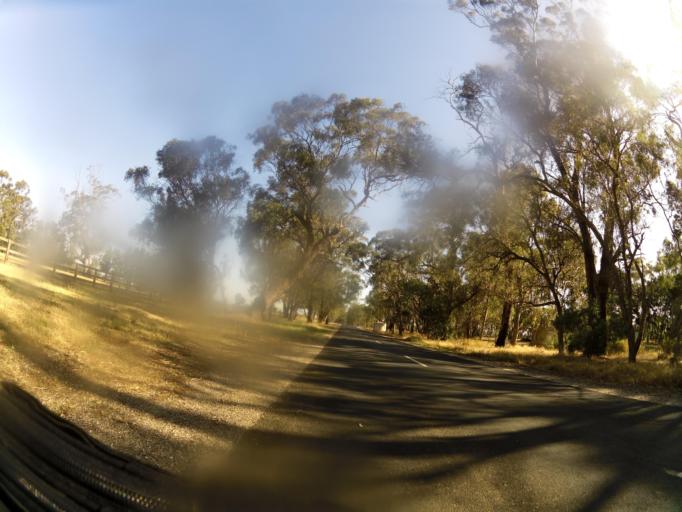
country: AU
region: Victoria
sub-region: Murrindindi
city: Kinglake West
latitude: -36.9612
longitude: 145.1079
